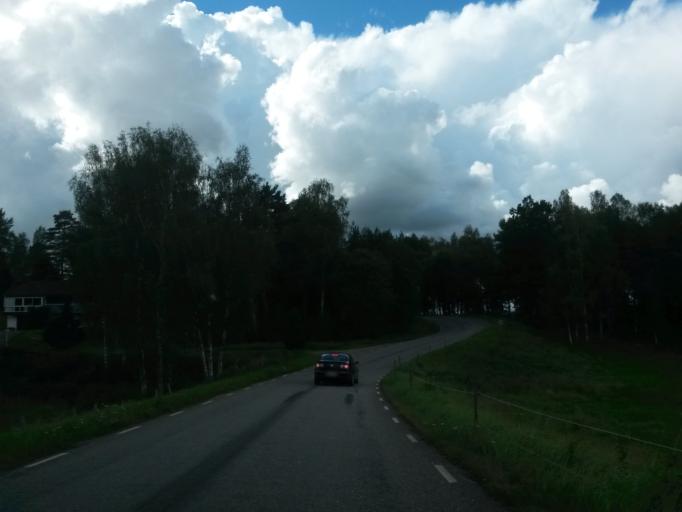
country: SE
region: Vaestra Goetaland
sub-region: Vargarda Kommun
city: Vargarda
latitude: 57.9907
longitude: 12.8051
